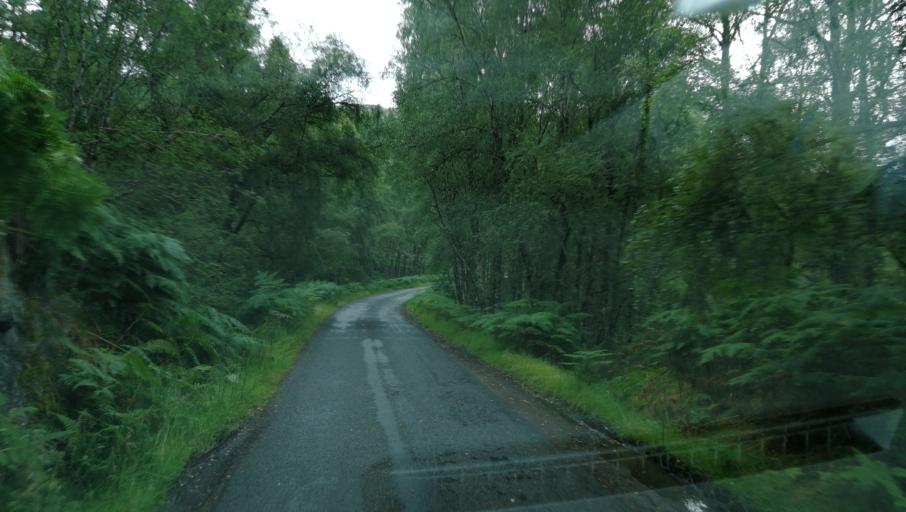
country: GB
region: Scotland
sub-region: Highland
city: Spean Bridge
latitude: 57.2996
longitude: -4.8980
